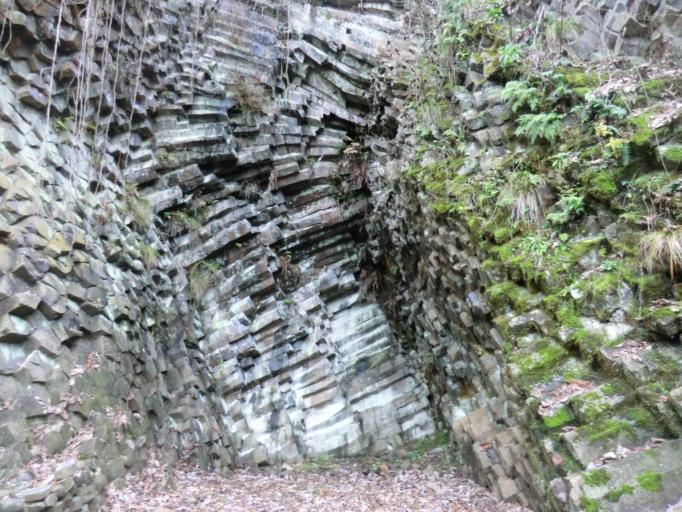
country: JP
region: Hyogo
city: Toyooka
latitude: 35.5890
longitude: 134.8045
